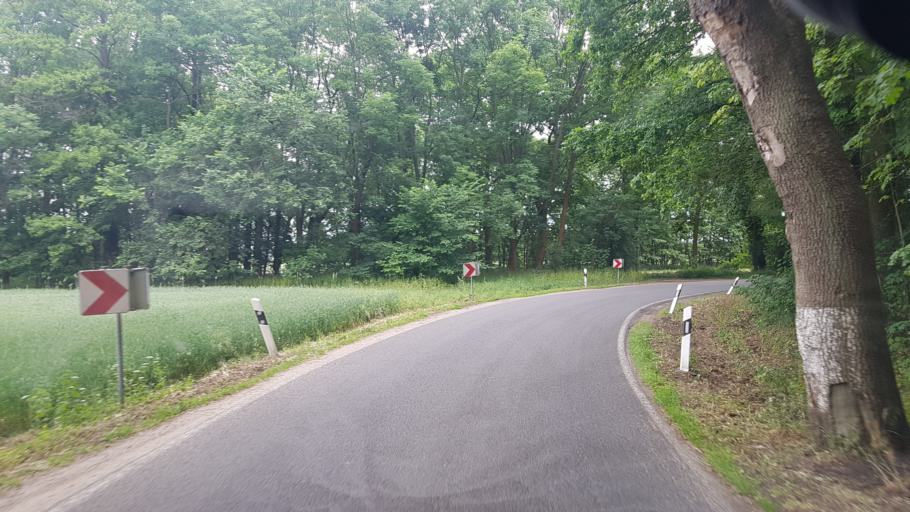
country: DE
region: Saxony-Anhalt
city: Holzdorf
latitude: 51.8020
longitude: 13.2357
